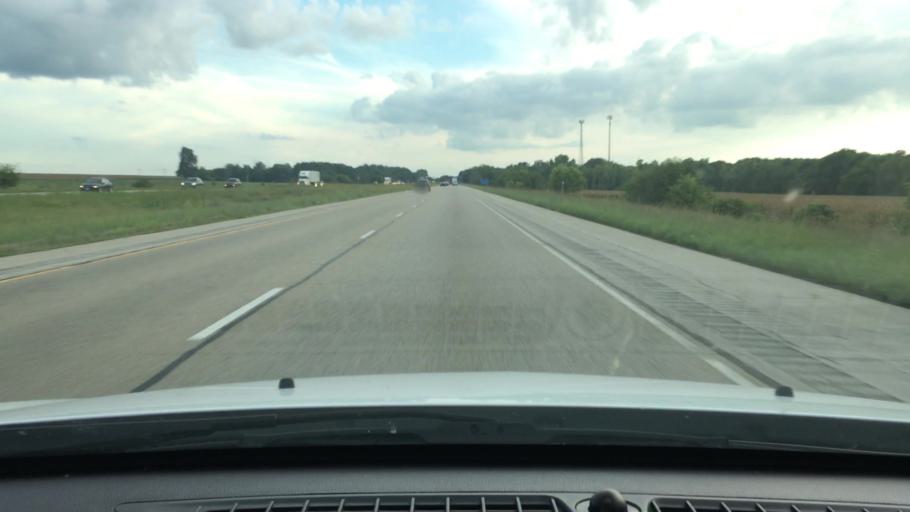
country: US
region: Illinois
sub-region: McLean County
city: Twin Grove
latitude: 40.3688
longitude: -89.1012
